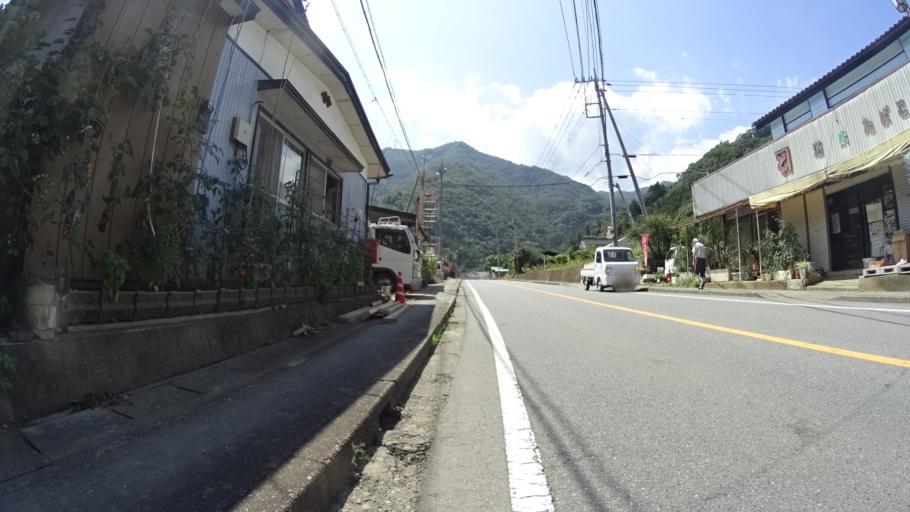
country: JP
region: Gunma
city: Tomioka
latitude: 36.0830
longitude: 138.7841
